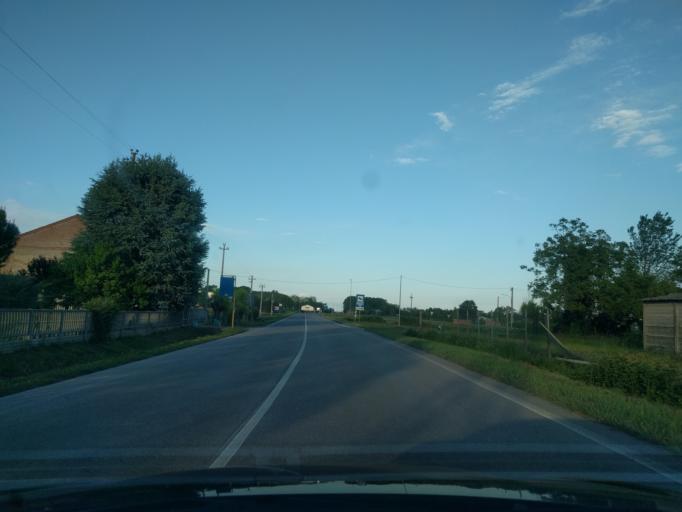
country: IT
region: Veneto
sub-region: Provincia di Rovigo
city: Crespino
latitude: 44.9871
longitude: 11.8769
